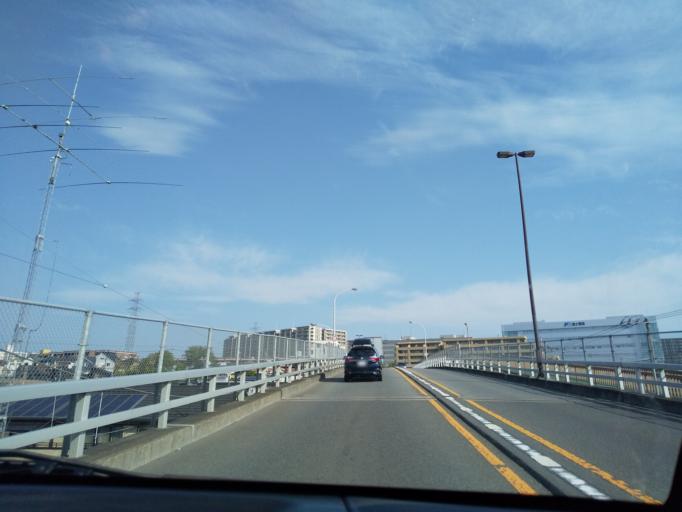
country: JP
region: Tokyo
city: Hino
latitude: 35.6563
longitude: 139.3778
